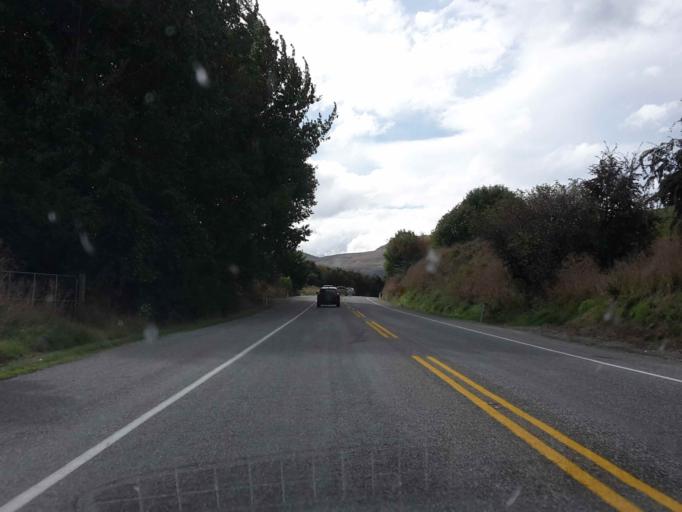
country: NZ
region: Otago
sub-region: Queenstown-Lakes District
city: Arrowtown
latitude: -44.9821
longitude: 168.8223
